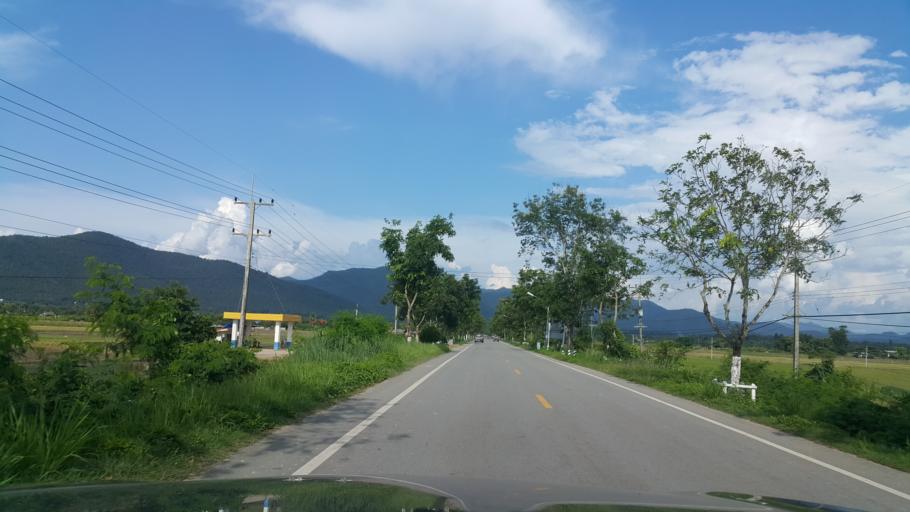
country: TH
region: Chiang Mai
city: Mae Taeng
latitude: 19.1444
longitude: 99.0196
